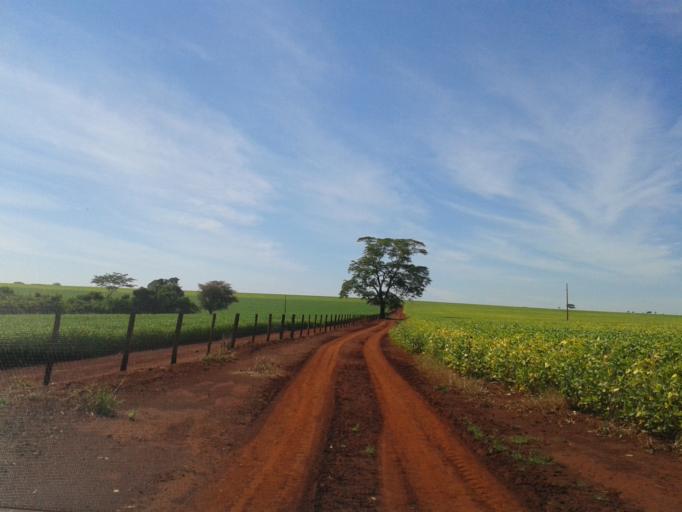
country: BR
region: Minas Gerais
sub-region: Capinopolis
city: Capinopolis
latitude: -18.6344
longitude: -49.7300
